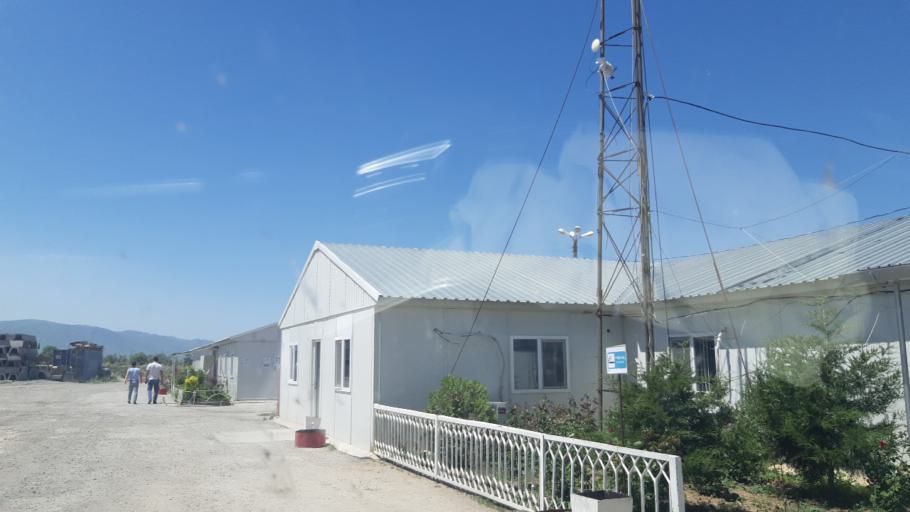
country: KZ
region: Ongtustik Qazaqstan
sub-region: Tulkibas Audany
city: Zhabagly
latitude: 42.5122
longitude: 70.4732
